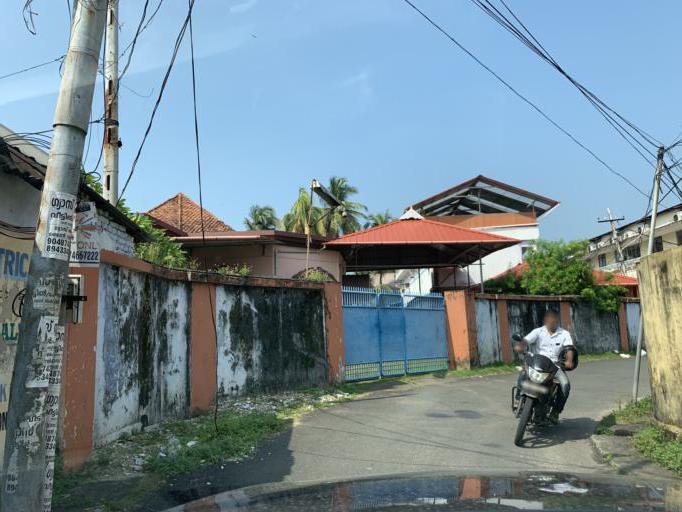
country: IN
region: Kerala
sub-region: Ernakulam
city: Cochin
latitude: 9.9572
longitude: 76.2554
